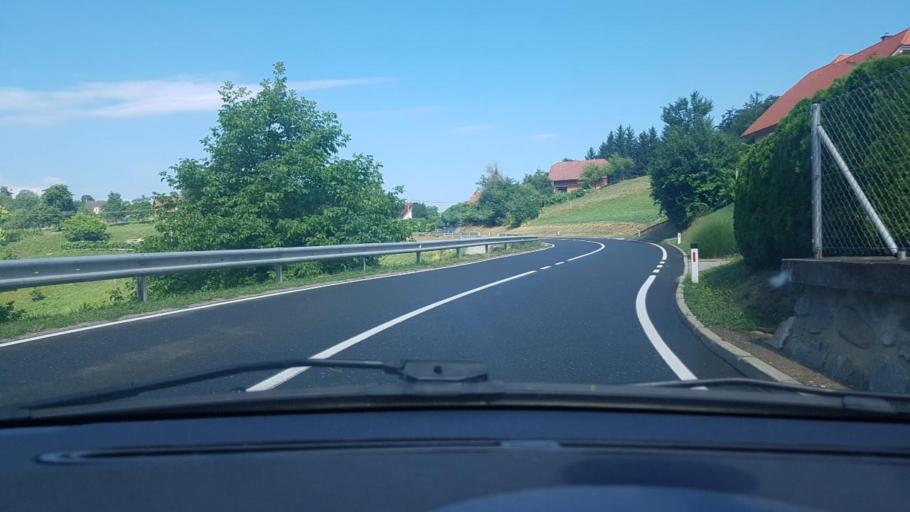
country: SI
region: Sentilj
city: Selnica ob Muri
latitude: 46.6901
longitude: 15.6768
